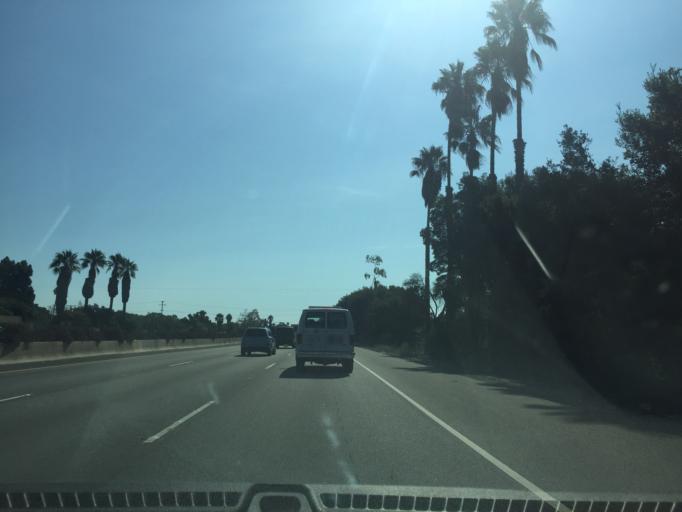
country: US
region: California
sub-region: Santa Barbara County
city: Santa Barbara
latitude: 34.4205
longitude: -119.7137
